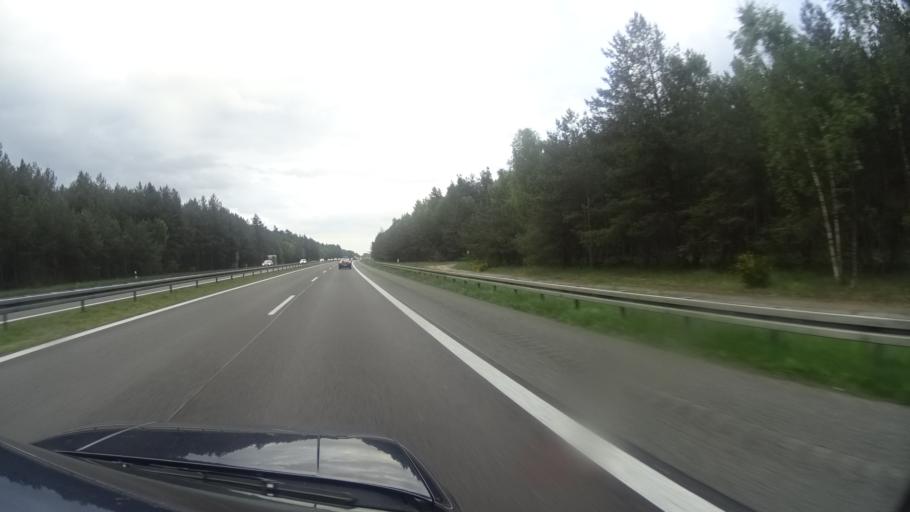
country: DE
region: Brandenburg
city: Walsleben
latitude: 53.0323
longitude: 12.5672
